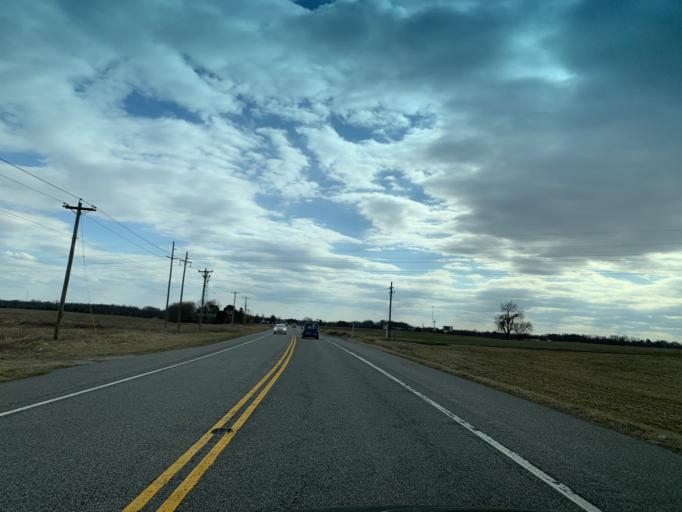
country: US
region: Maryland
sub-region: Queen Anne's County
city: Centreville
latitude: 38.9649
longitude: -76.0776
